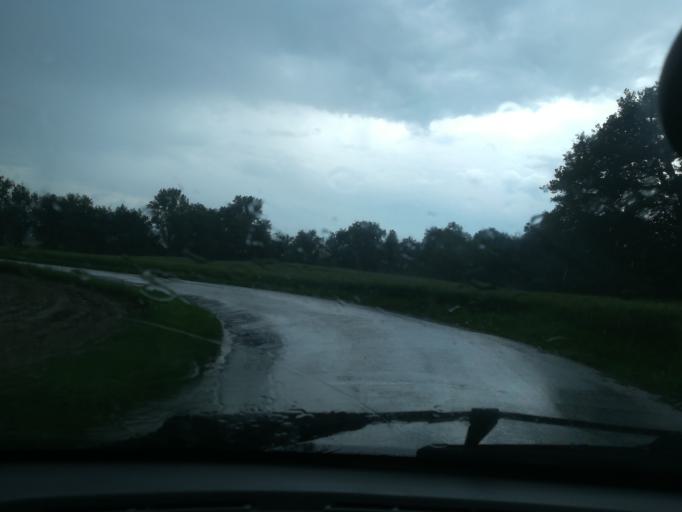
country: IT
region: The Marches
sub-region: Provincia di Macerata
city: Passo di Treia
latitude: 43.3077
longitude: 13.3457
